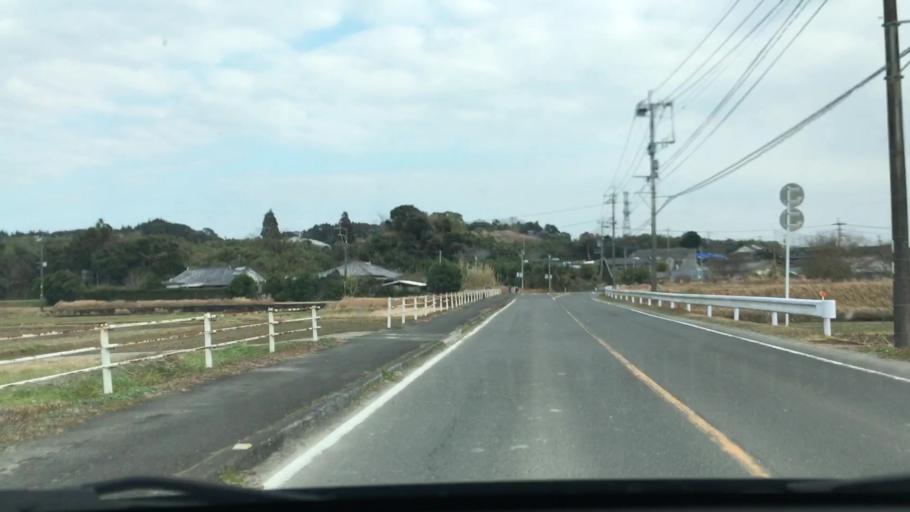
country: JP
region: Miyazaki
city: Kushima
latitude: 31.4679
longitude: 131.2132
